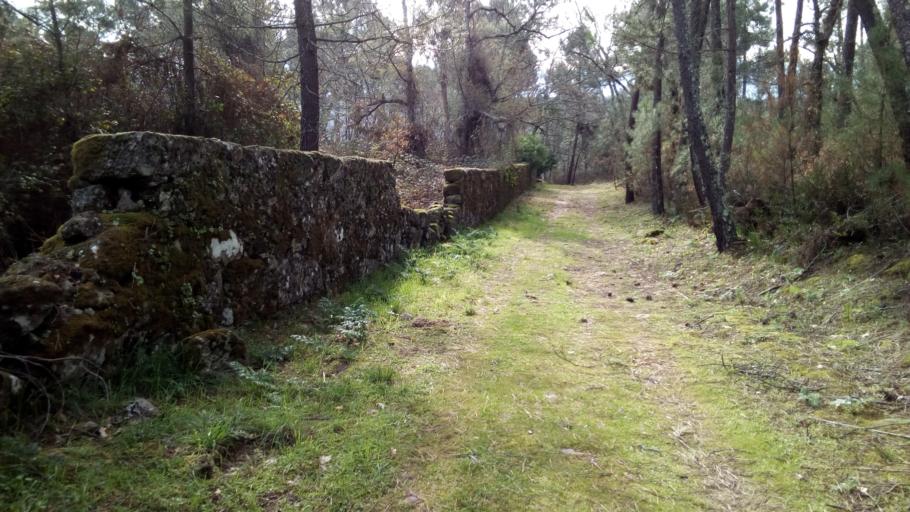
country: PT
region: Guarda
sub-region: Fornos de Algodres
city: Fornos de Algodres
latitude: 40.6125
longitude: -7.5303
